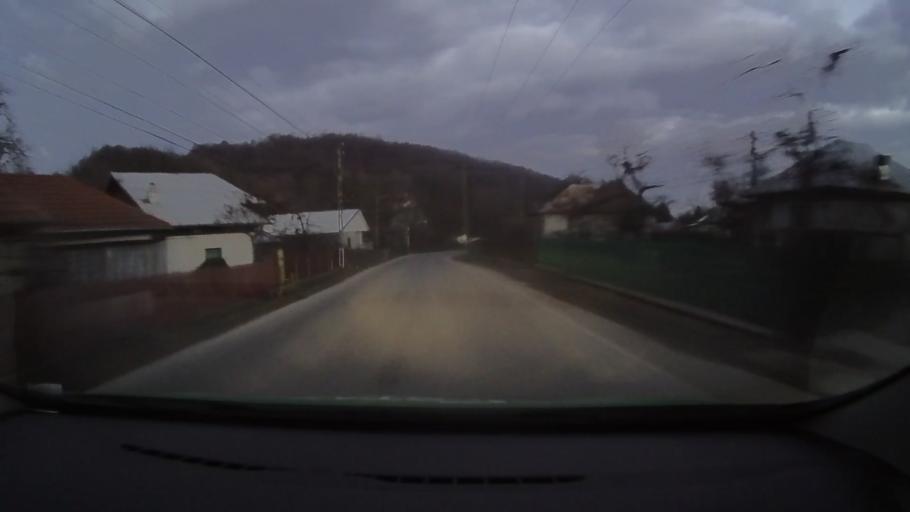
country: RO
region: Prahova
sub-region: Comuna Provita de Jos
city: Provita de Jos
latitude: 45.1290
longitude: 25.6494
